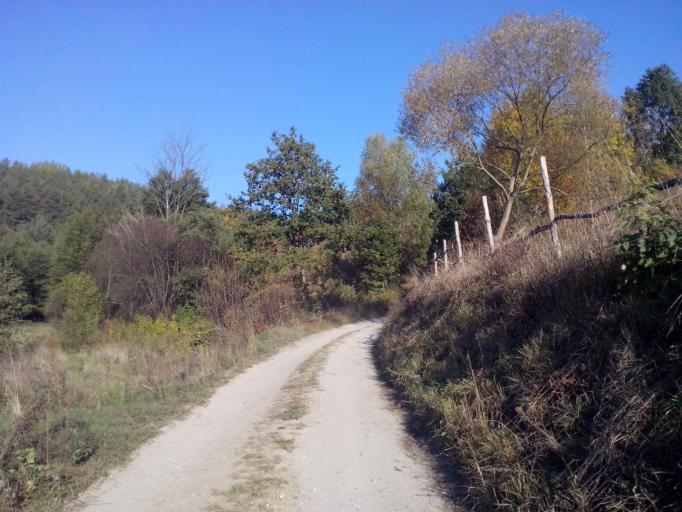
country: PL
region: Kujawsko-Pomorskie
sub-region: Powiat brodnicki
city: Gorzno
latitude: 53.2095
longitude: 19.6472
